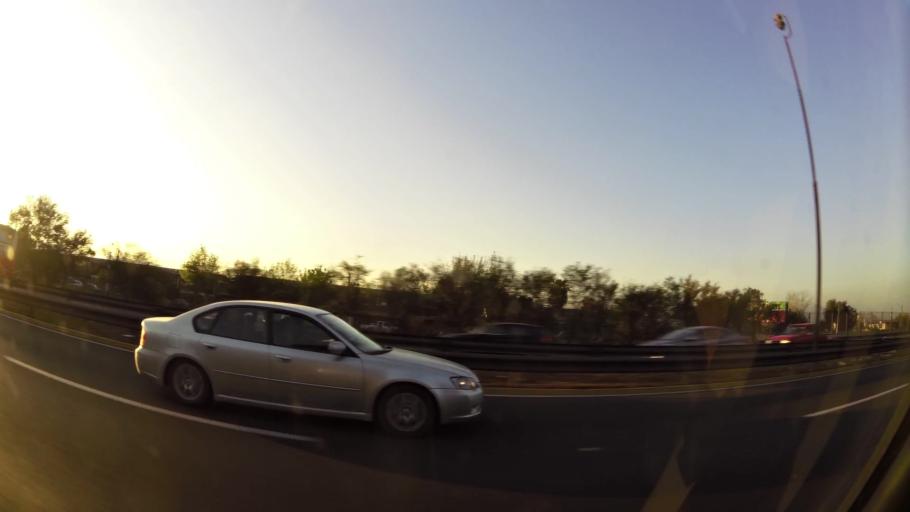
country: CL
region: Santiago Metropolitan
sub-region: Provincia de Santiago
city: Lo Prado
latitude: -33.4788
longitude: -70.6947
